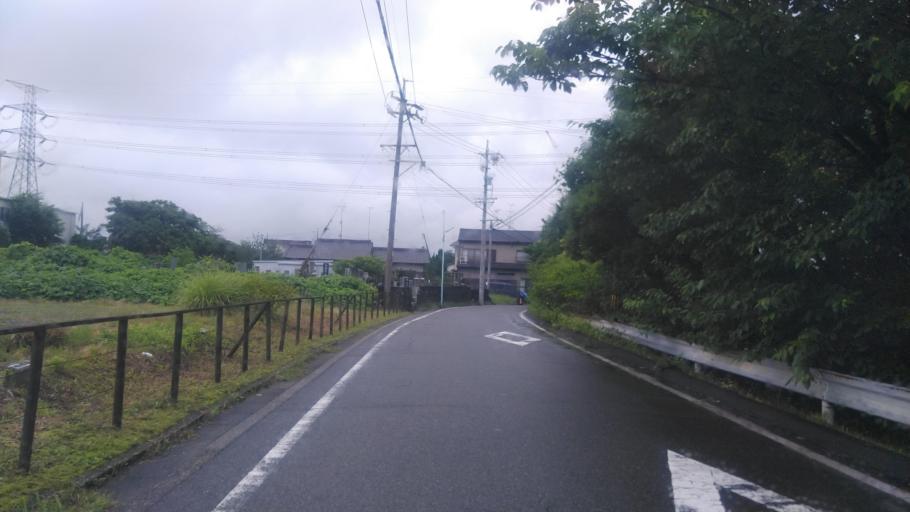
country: JP
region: Aichi
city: Kasugai
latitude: 35.2477
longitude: 137.0323
